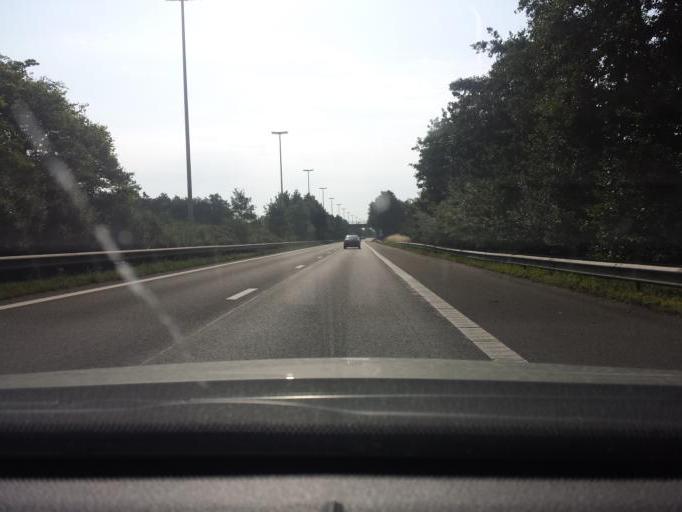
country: BE
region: Flanders
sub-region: Provincie Limburg
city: Diepenbeek
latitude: 50.8968
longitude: 5.3927
